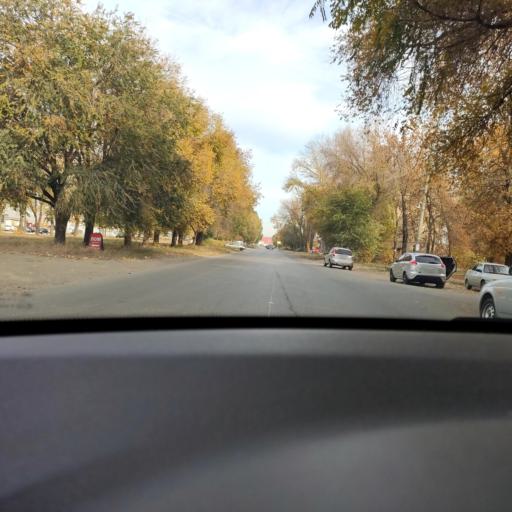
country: RU
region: Samara
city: Petra-Dubrava
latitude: 53.2476
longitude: 50.3097
